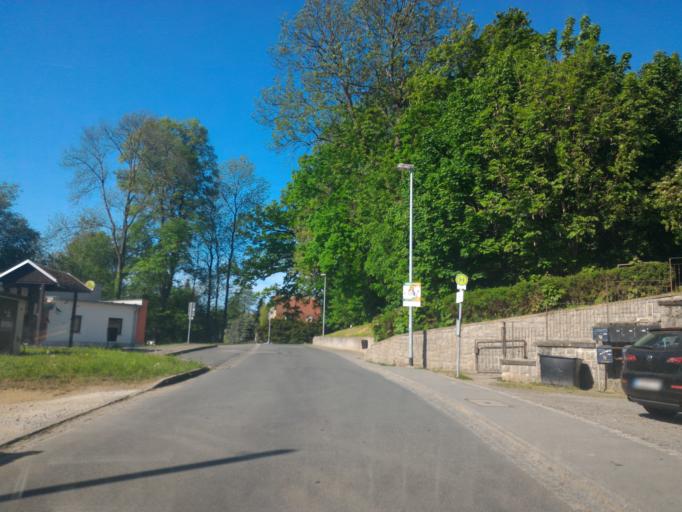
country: DE
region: Saxony
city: Grossschweidnitz
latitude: 51.0677
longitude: 14.6404
